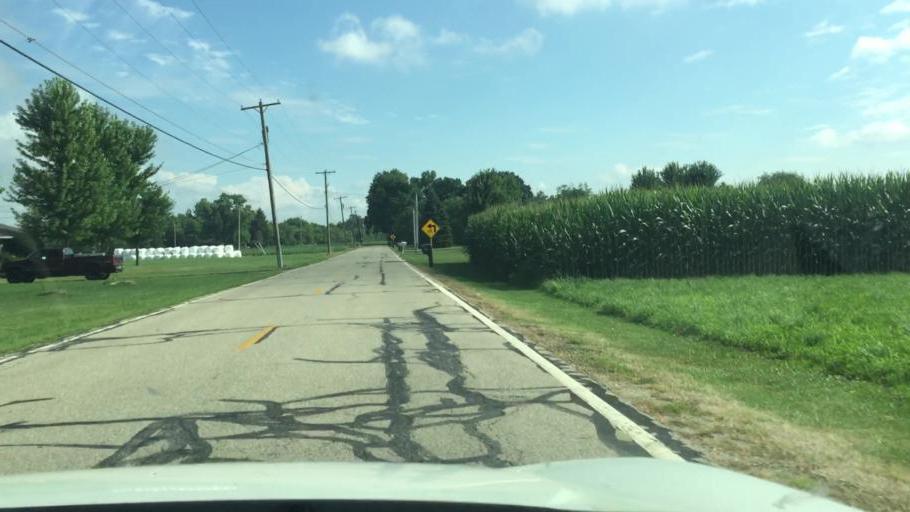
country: US
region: Ohio
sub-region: Clark County
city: Northridge
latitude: 40.0023
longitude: -83.7136
